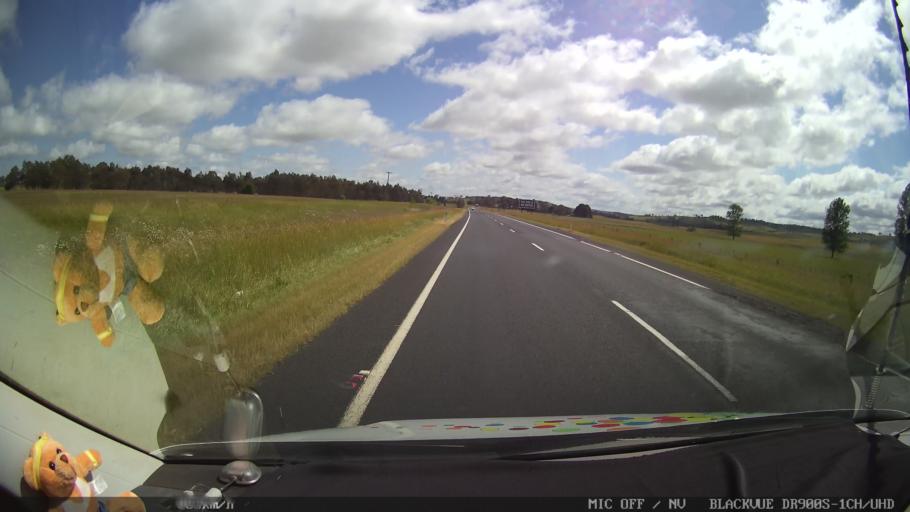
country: AU
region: New South Wales
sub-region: Glen Innes Severn
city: Glen Innes
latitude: -29.9171
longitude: 151.7274
